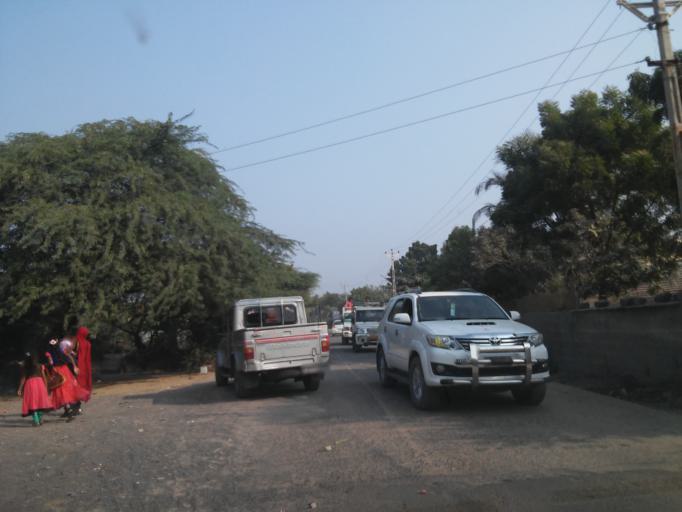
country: IN
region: Gujarat
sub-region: Kachchh
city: Mundra
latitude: 22.8352
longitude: 69.6534
